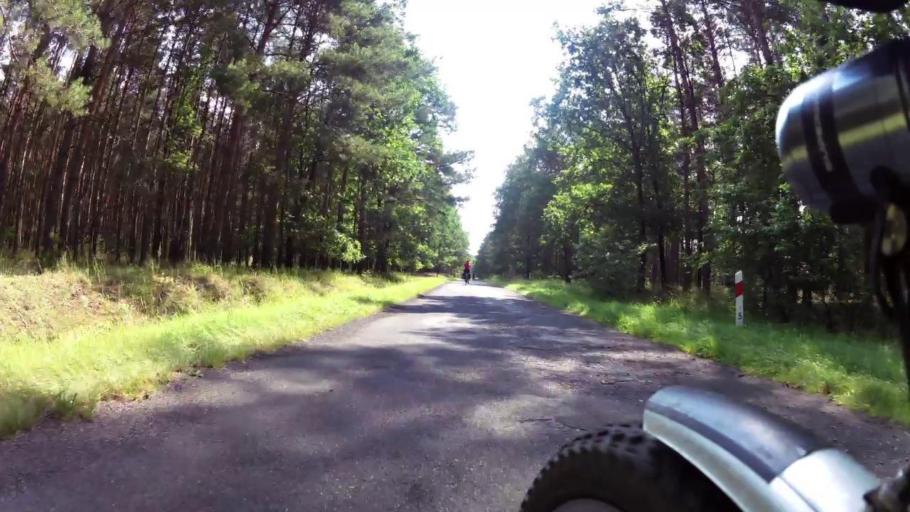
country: PL
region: West Pomeranian Voivodeship
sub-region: Powiat mysliborski
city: Boleszkowice
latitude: 52.6753
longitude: 14.5082
